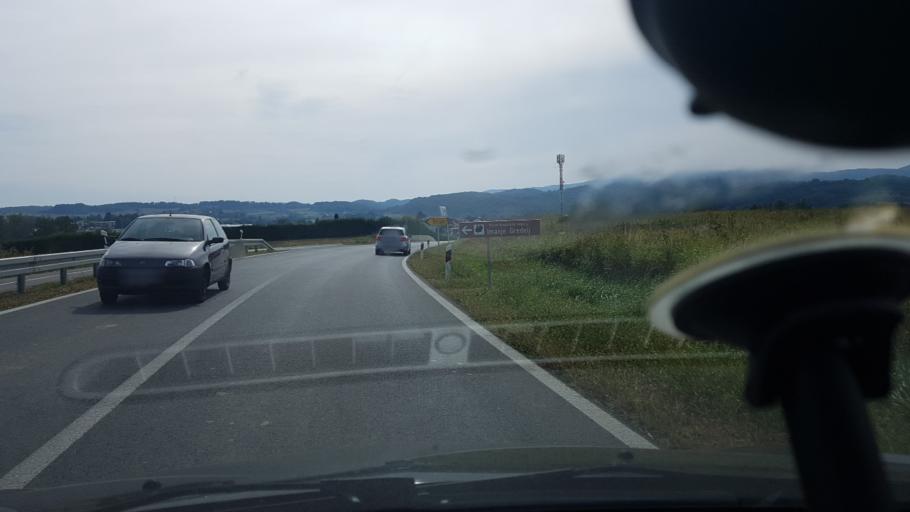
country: HR
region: Krapinsko-Zagorska
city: Marija Bistrica
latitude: 46.0571
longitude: 16.1640
